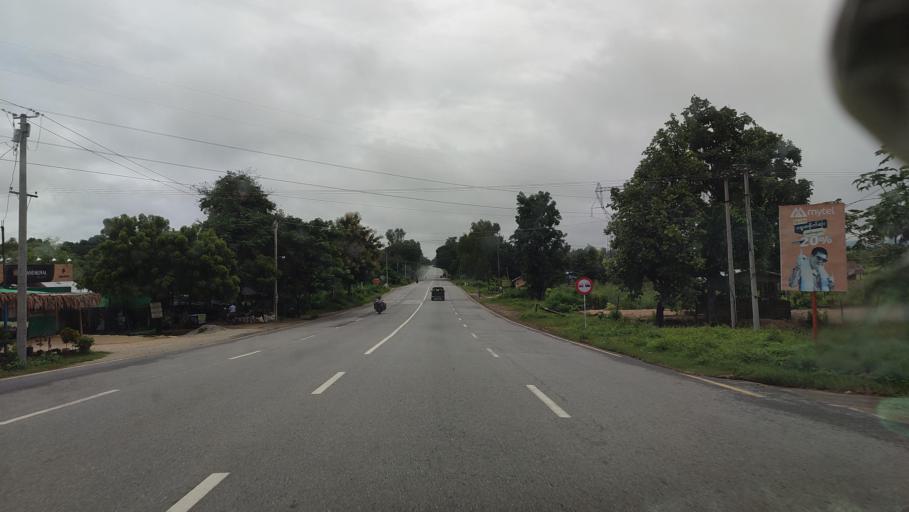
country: MM
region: Mandalay
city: Pyinmana
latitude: 19.9940
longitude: 96.2476
